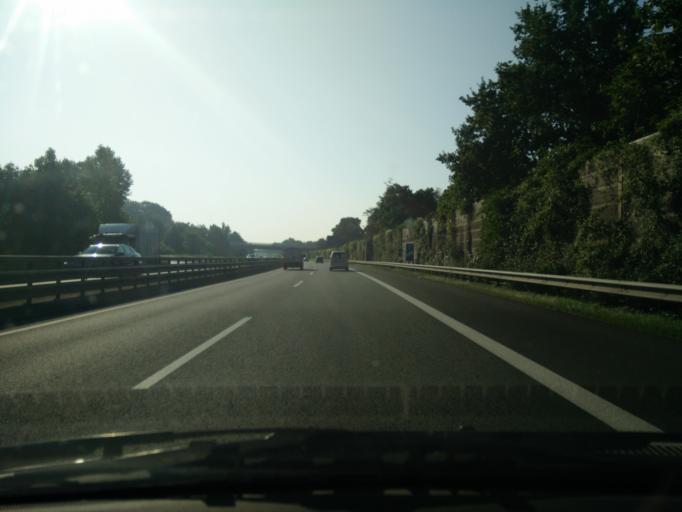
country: DE
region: Schleswig-Holstein
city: Halstenbek
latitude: 53.6417
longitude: 9.8352
